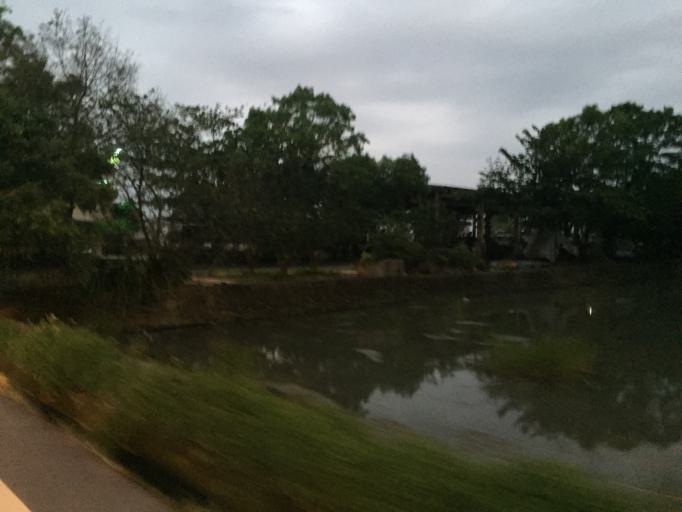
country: TW
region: Taiwan
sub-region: Yilan
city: Yilan
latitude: 24.7712
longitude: 121.7442
